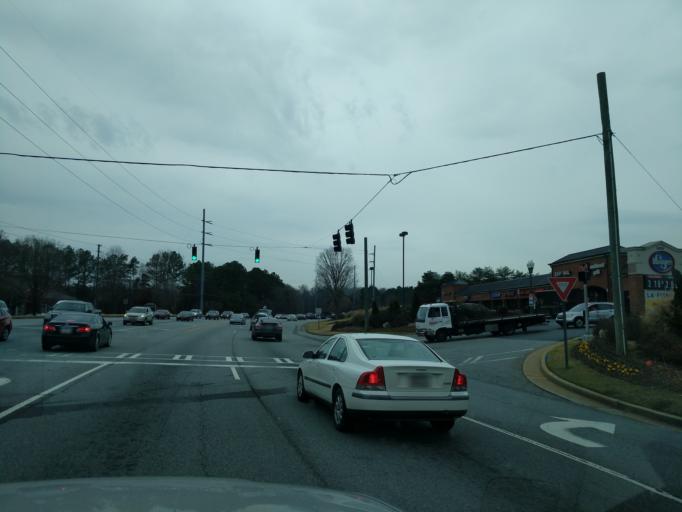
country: US
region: Georgia
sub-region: Gwinnett County
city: Berkeley Lake
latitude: 34.0046
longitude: -84.1722
